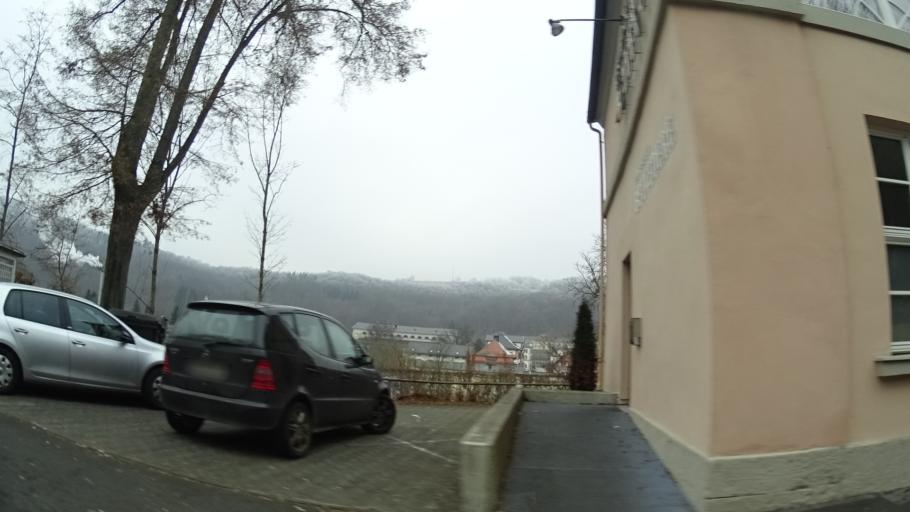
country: DE
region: Bavaria
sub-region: Regierungsbezirk Unterfranken
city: Bad Bruckenau
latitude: 50.3011
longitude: 9.7498
